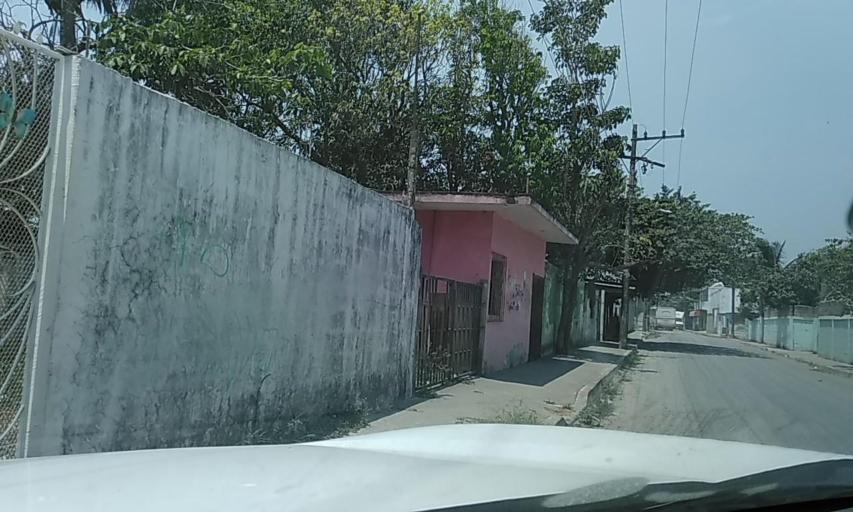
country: MX
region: Veracruz
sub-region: Veracruz
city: Las Amapolas
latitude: 19.1410
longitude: -96.1996
